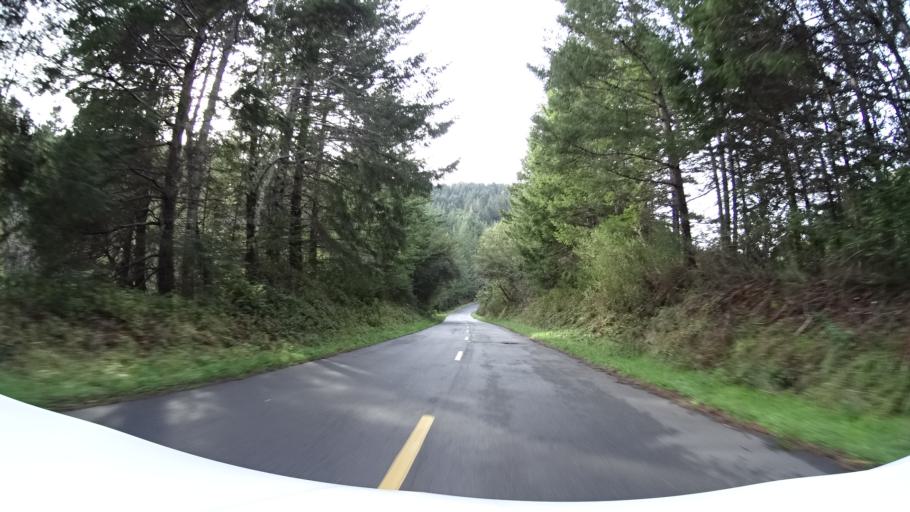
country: US
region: California
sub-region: Humboldt County
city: Ferndale
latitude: 40.3462
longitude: -124.3394
